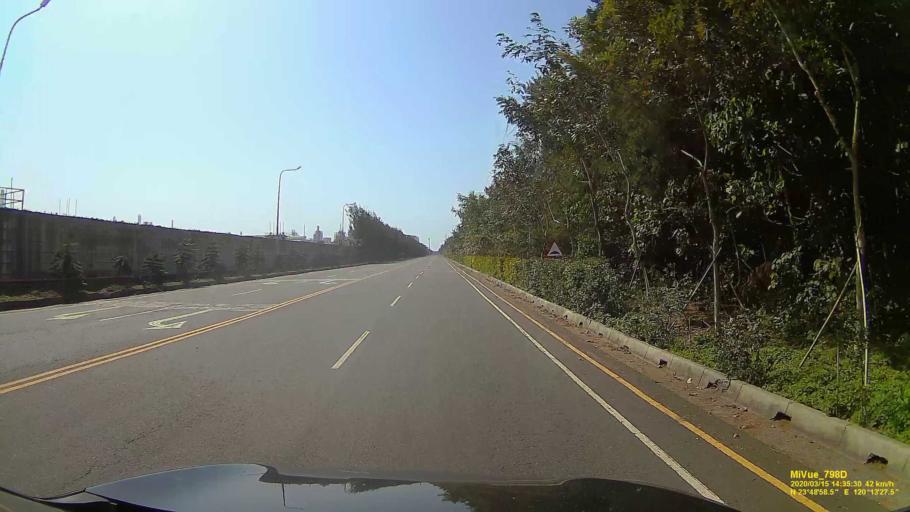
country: TW
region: Taiwan
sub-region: Yunlin
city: Douliu
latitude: 23.8163
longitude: 120.2240
